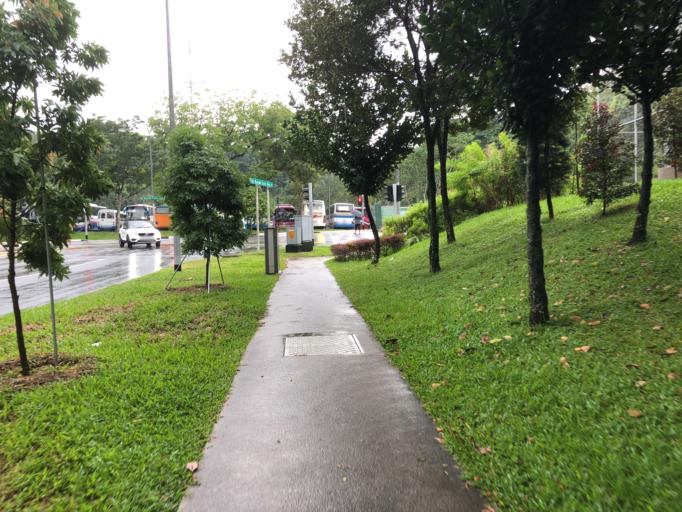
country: SG
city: Singapore
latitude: 1.3495
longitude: 103.7604
